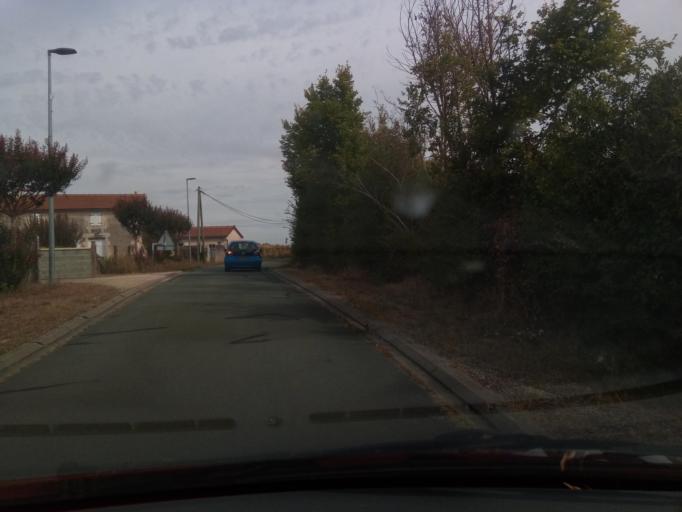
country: FR
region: Poitou-Charentes
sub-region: Departement de la Vienne
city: Montmorillon
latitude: 46.4927
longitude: 0.8127
